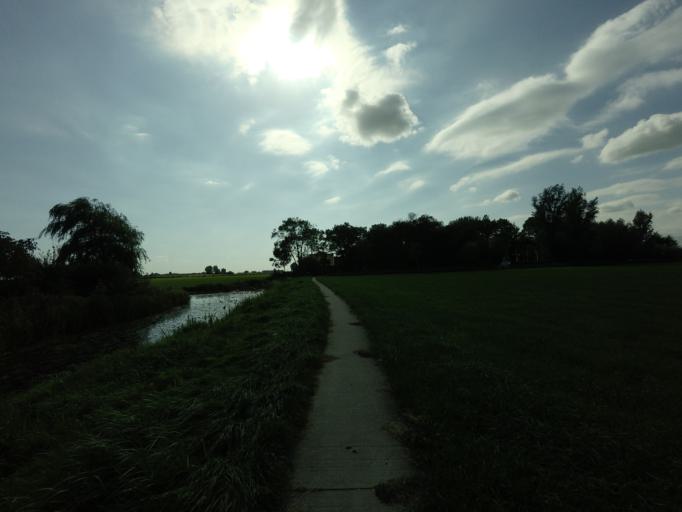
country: NL
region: Friesland
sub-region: Gemeente Littenseradiel
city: Makkum
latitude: 53.0898
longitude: 5.6350
